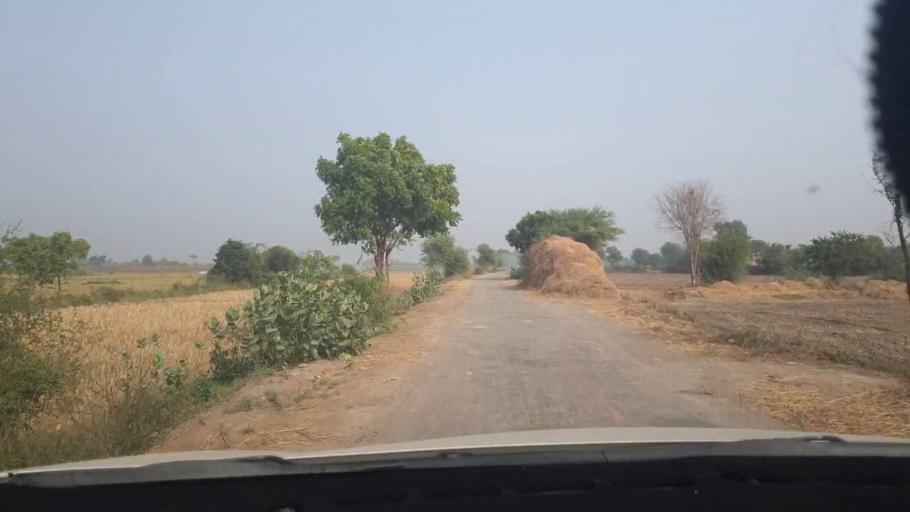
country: PK
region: Sindh
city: Tando Muhammad Khan
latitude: 24.9712
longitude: 68.4870
